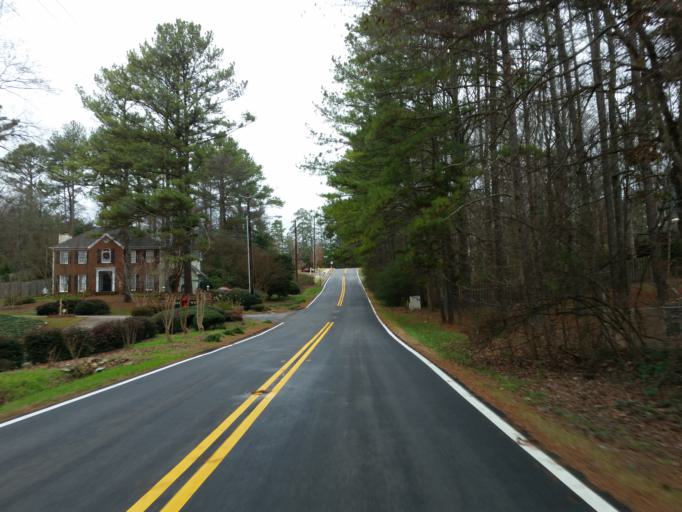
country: US
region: Georgia
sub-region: Cherokee County
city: Woodstock
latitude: 34.0405
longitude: -84.4853
